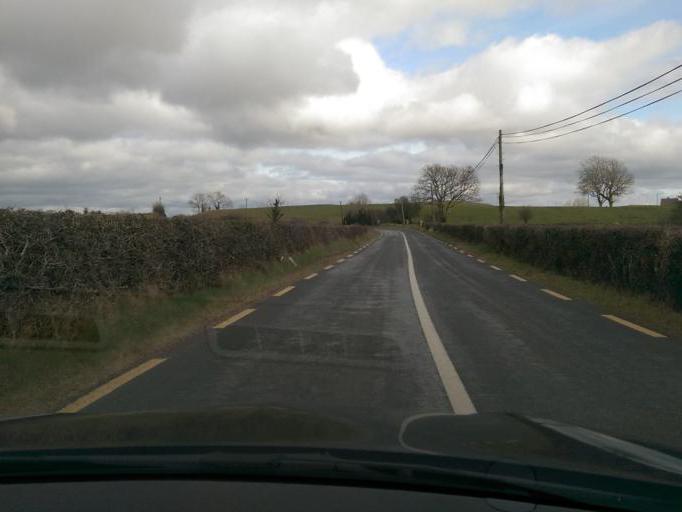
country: IE
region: Connaught
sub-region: County Galway
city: Loughrea
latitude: 53.3243
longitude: -8.4279
